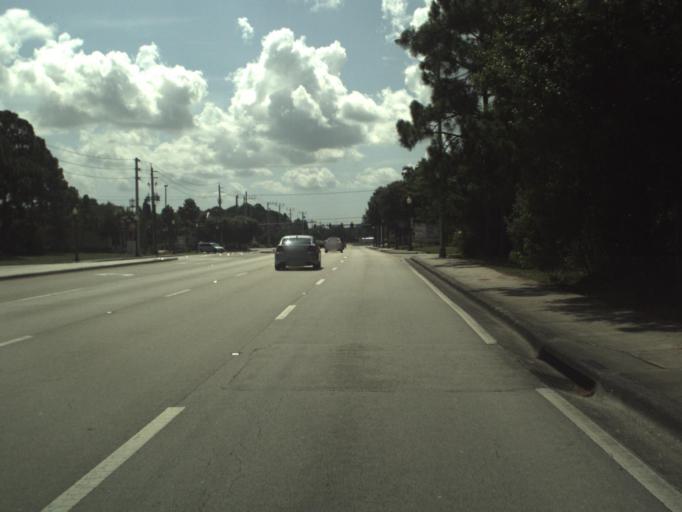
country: US
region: Florida
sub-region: Saint Lucie County
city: Port Saint Lucie
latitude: 27.2591
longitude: -80.3774
